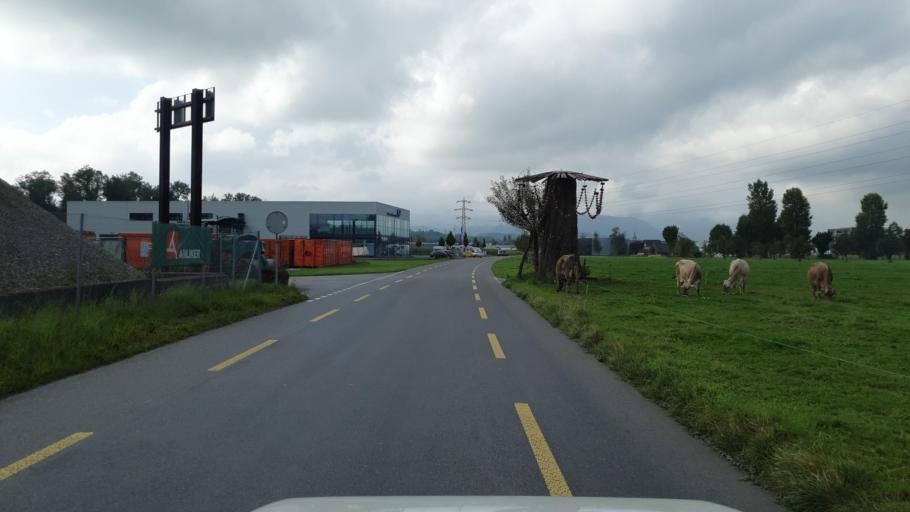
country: CH
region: Lucerne
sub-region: Lucerne-Land District
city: Ebikon
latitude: 47.0893
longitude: 8.3164
